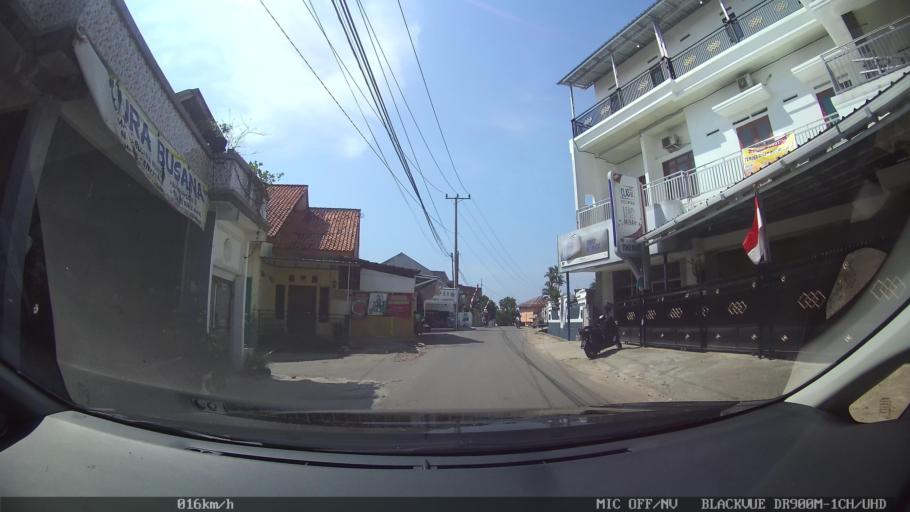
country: ID
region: Lampung
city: Kedaton
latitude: -5.3730
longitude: 105.2507
